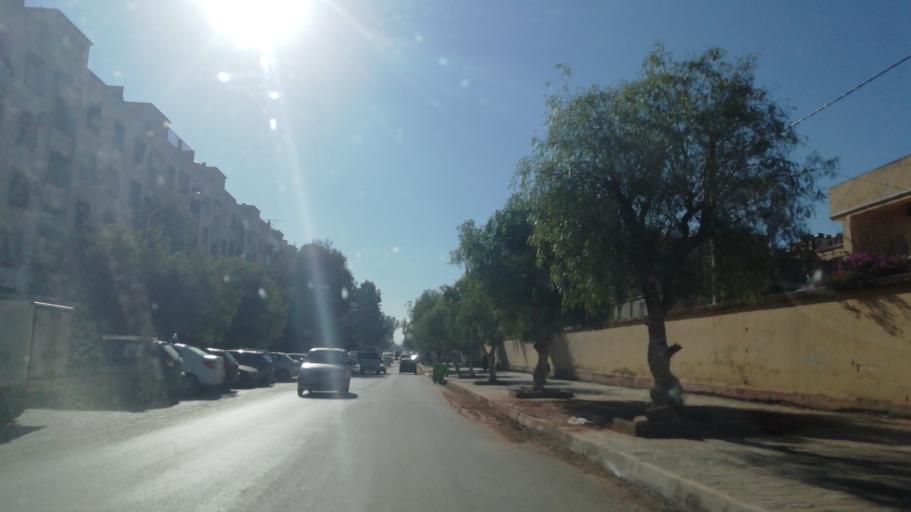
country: DZ
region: Oran
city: Oran
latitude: 35.6720
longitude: -0.6500
